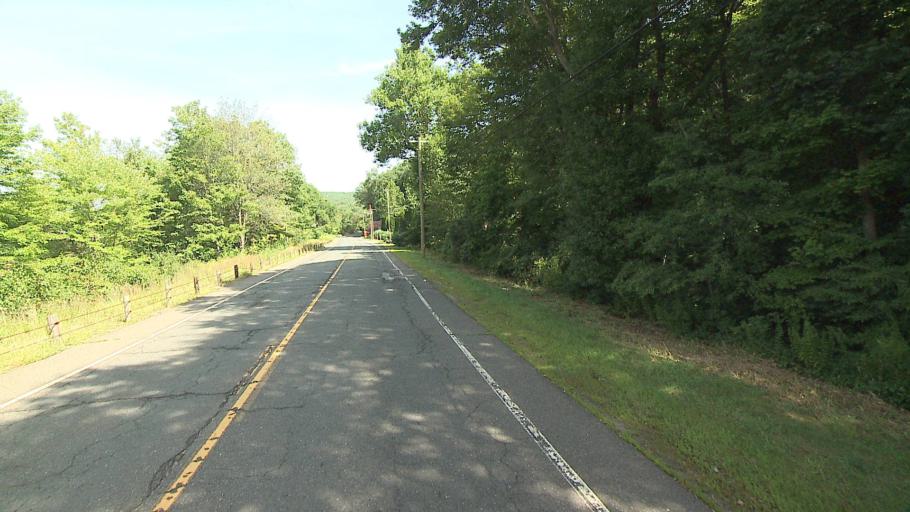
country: US
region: Connecticut
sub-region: Litchfield County
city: Oakville
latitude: 41.6123
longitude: -73.0579
